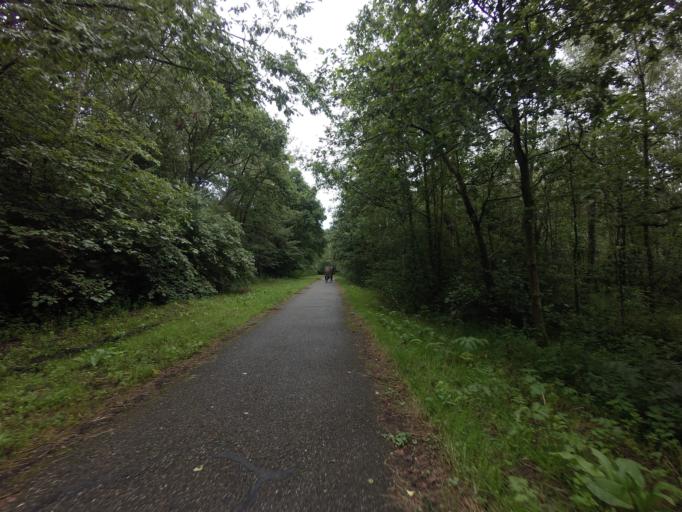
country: NL
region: North Holland
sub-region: Gemeente Velsen
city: Velsen-Zuid
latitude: 52.4313
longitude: 4.7122
